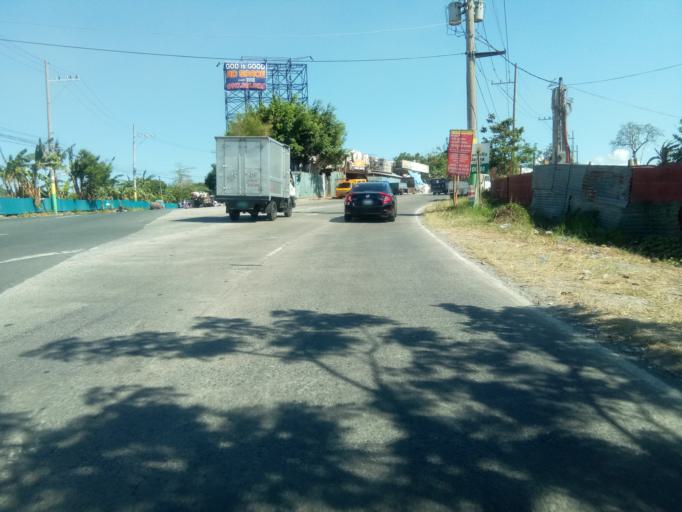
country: PH
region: Calabarzon
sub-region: Province of Cavite
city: Bulihan
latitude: 14.3132
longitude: 120.9876
